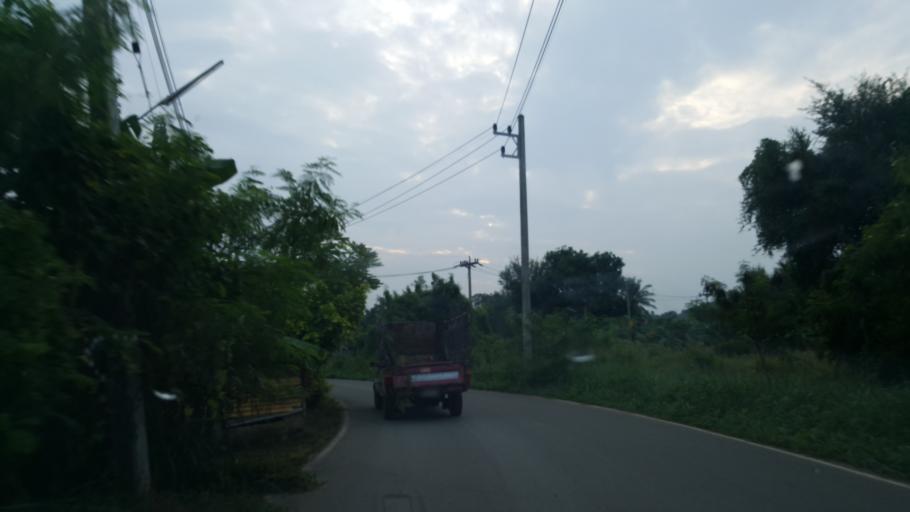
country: TH
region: Chon Buri
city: Sattahip
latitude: 12.7137
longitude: 100.9159
